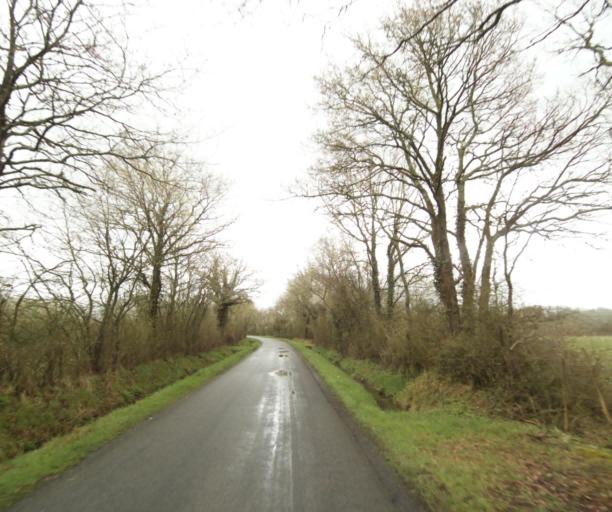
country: FR
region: Pays de la Loire
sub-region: Departement de la Loire-Atlantique
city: Quilly
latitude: 47.4600
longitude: -1.8947
